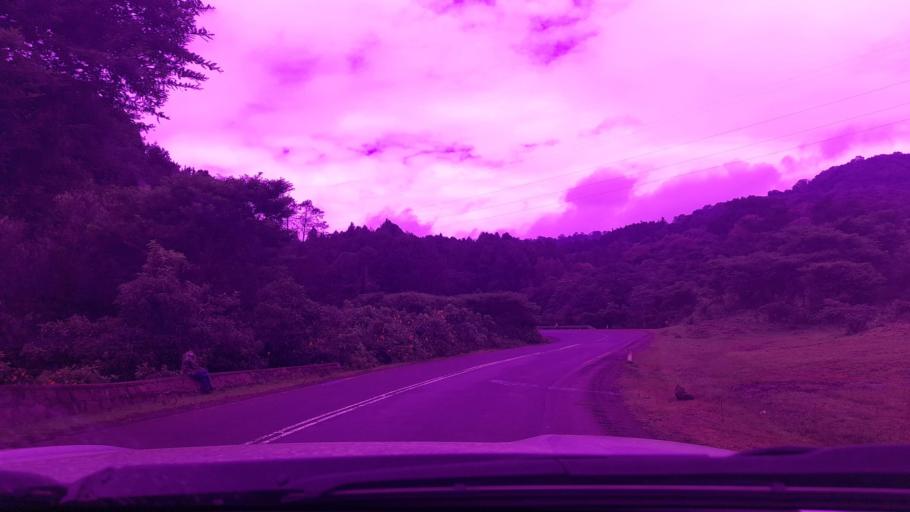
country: ET
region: Oromiya
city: Jima
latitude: 7.5574
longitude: 36.5961
